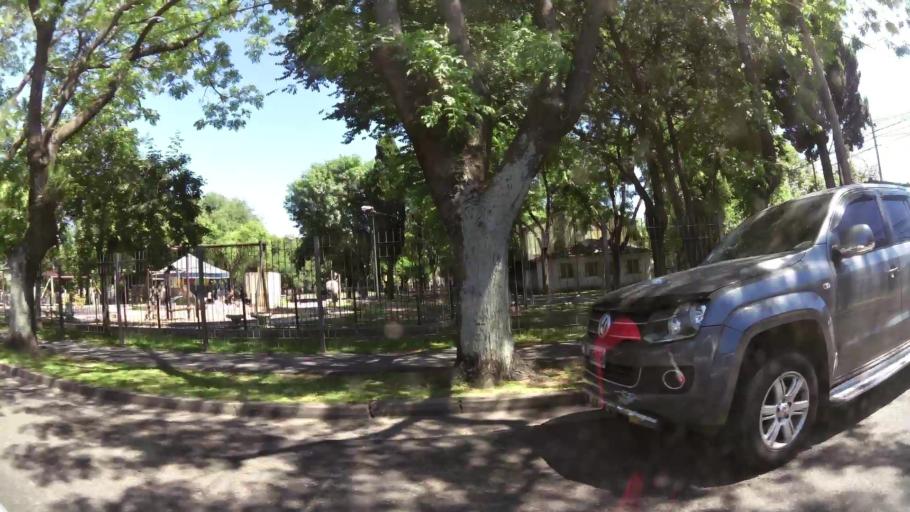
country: AR
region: Buenos Aires
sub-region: Partido de General San Martin
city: General San Martin
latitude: -34.5303
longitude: -58.5500
